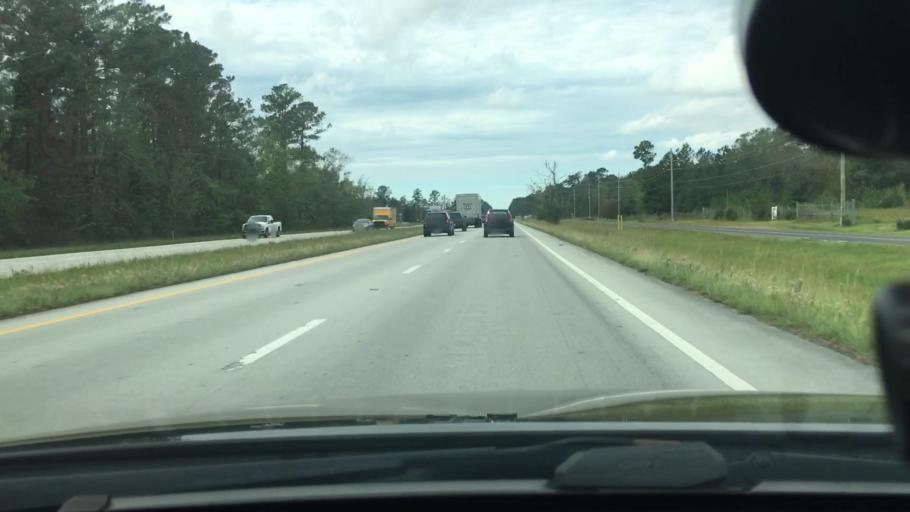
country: US
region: North Carolina
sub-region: Craven County
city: Neuse Forest
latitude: 35.0046
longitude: -76.9889
